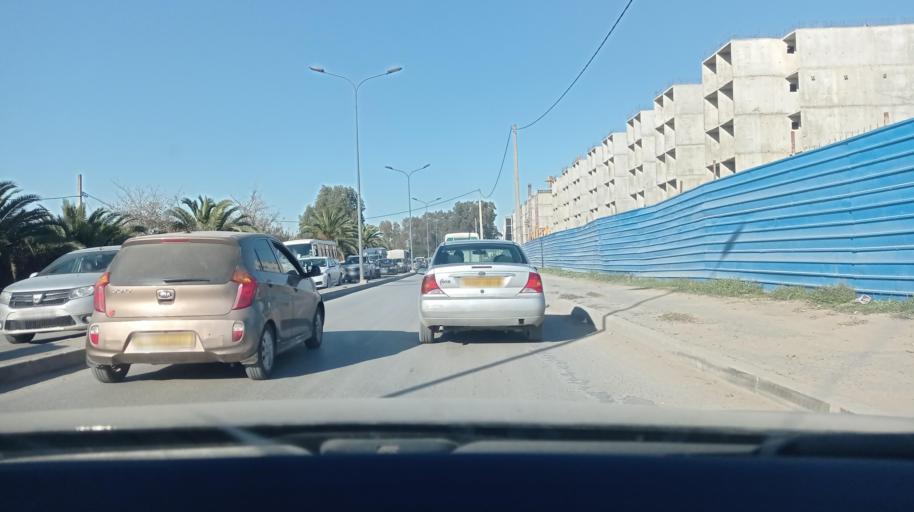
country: DZ
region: Tipaza
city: Baraki
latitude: 36.6560
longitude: 3.0857
